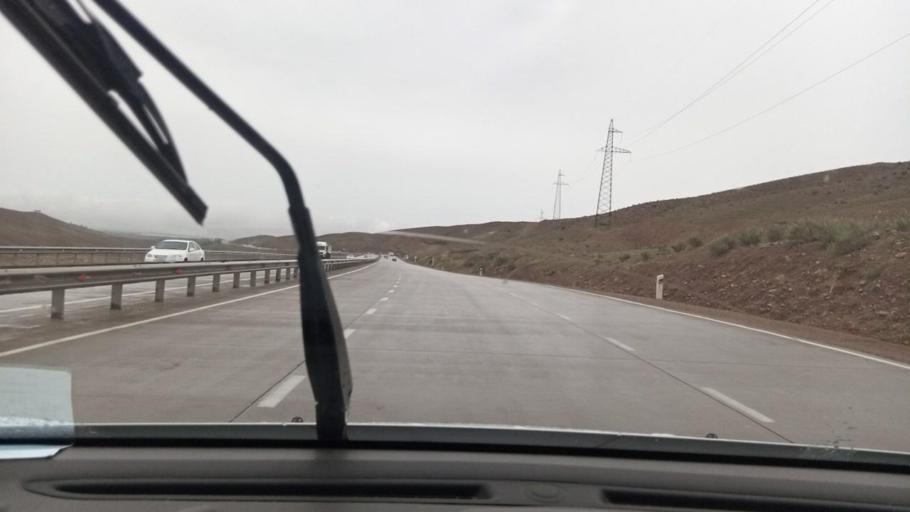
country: UZ
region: Namangan
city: Pop Shahri
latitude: 40.9344
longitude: 70.6973
